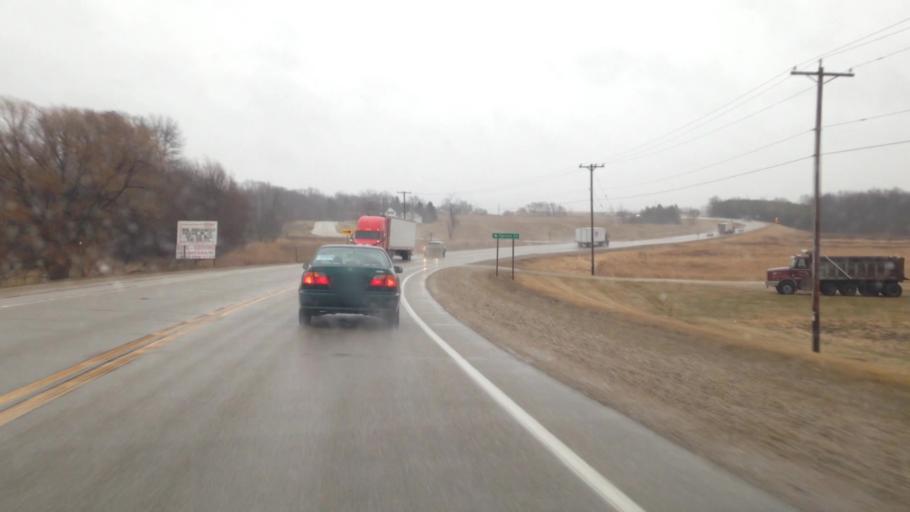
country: US
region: Wisconsin
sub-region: Washington County
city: Hartford
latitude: 43.4234
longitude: -88.3846
